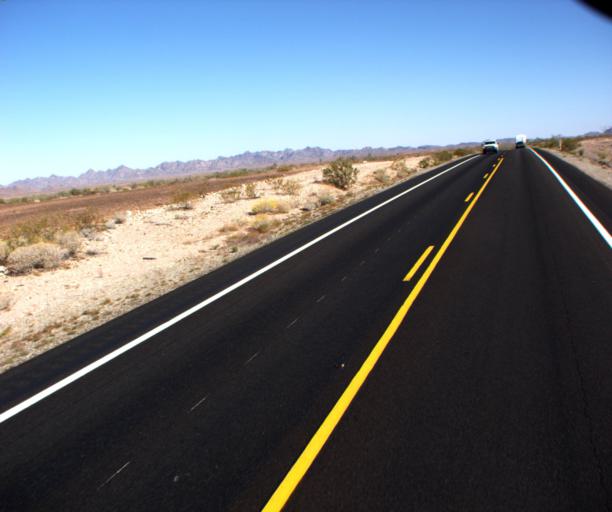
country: US
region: Arizona
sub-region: Yuma County
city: Wellton
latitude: 33.1234
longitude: -114.2913
